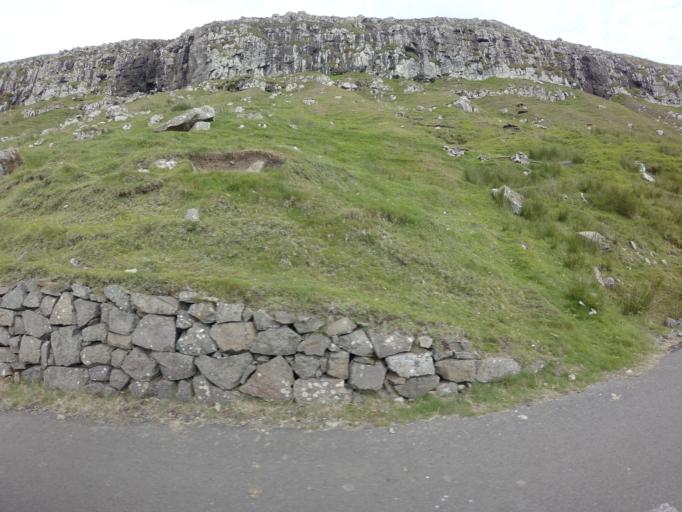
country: FO
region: Sandoy
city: Sandur
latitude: 61.8358
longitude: -6.7932
